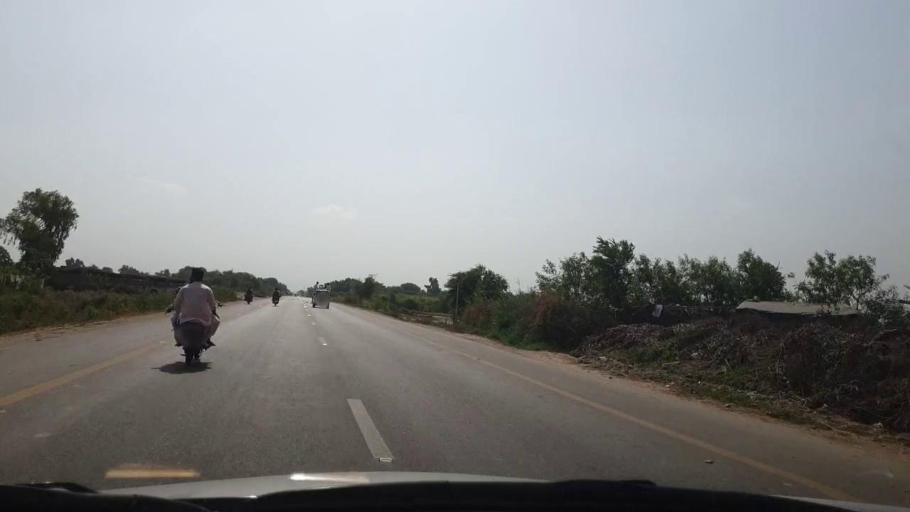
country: PK
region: Sindh
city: Matli
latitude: 25.0671
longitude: 68.6278
